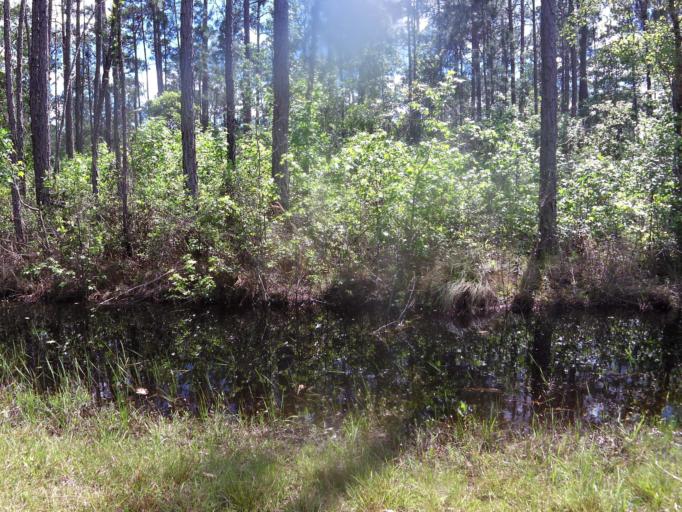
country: US
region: Florida
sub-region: Clay County
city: Green Cove Springs
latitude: 29.9650
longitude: -81.6365
